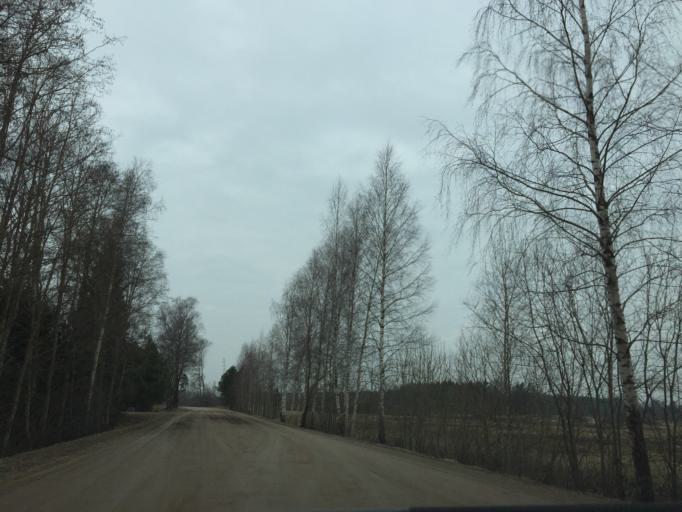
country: LV
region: Kekava
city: Kekava
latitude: 56.8051
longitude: 24.1697
